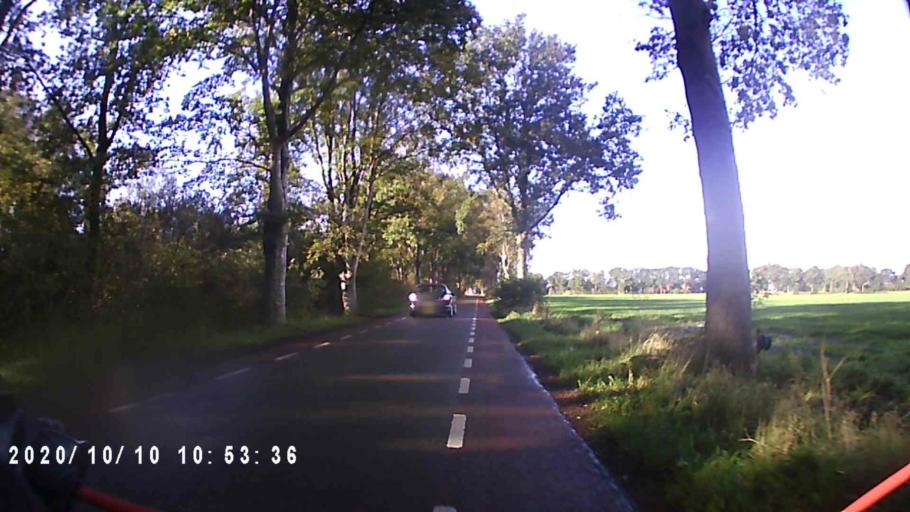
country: NL
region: Friesland
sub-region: Gemeente Achtkarspelen
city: Surhuisterveen
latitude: 53.1562
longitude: 6.2172
